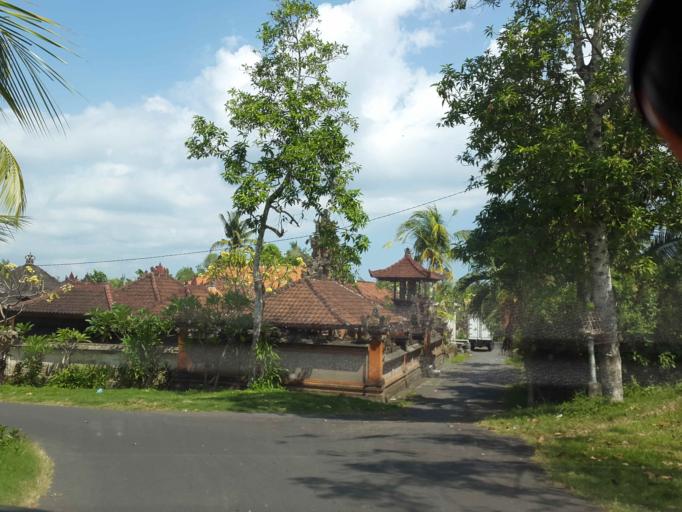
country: ID
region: Bali
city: Klungkung
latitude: -8.5580
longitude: 115.3806
